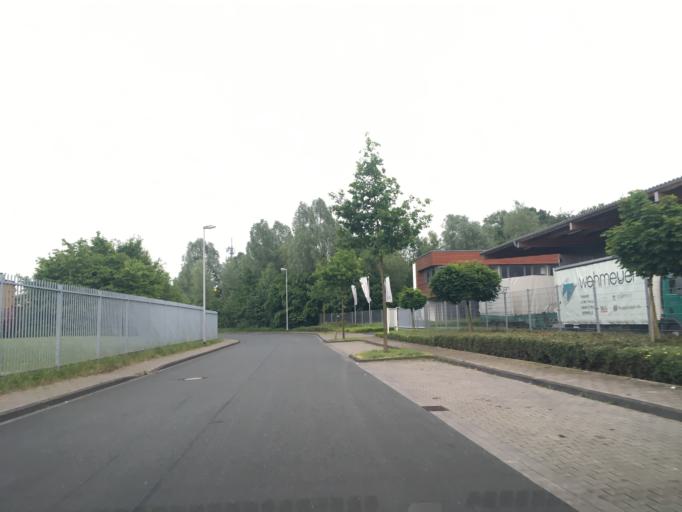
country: DE
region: North Rhine-Westphalia
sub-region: Regierungsbezirk Munster
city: Muenster
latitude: 51.9907
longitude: 7.5647
